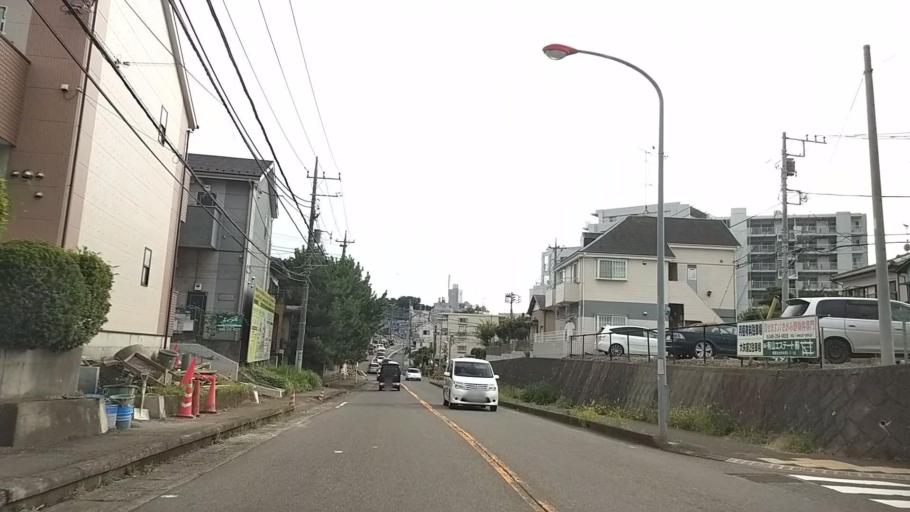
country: JP
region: Kanagawa
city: Minami-rinkan
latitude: 35.4705
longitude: 139.4219
